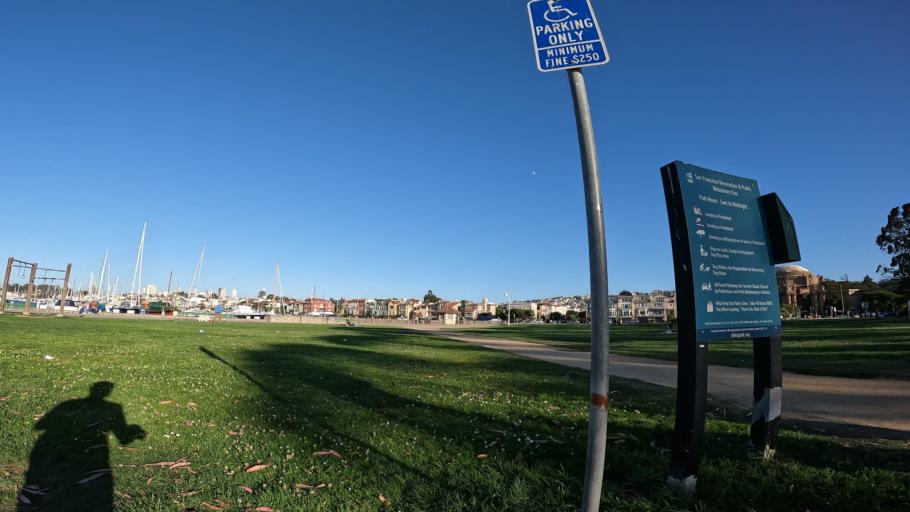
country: US
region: California
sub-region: San Francisco County
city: San Francisco
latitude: 37.8064
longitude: -122.4480
